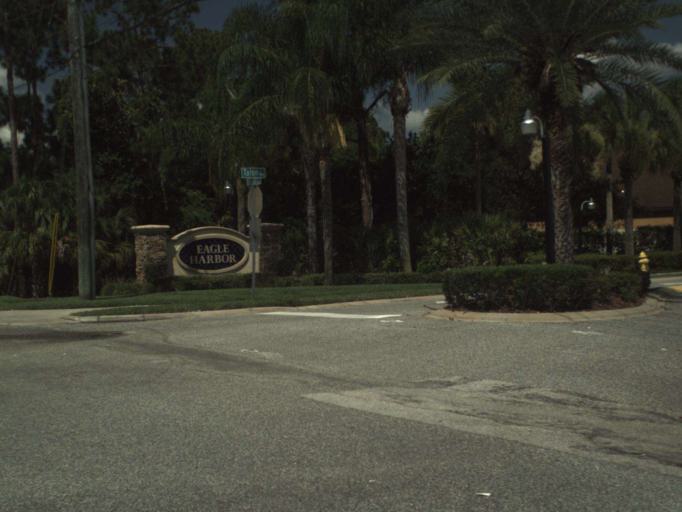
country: US
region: Florida
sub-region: Brevard County
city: June Park
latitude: 28.1251
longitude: -80.6894
